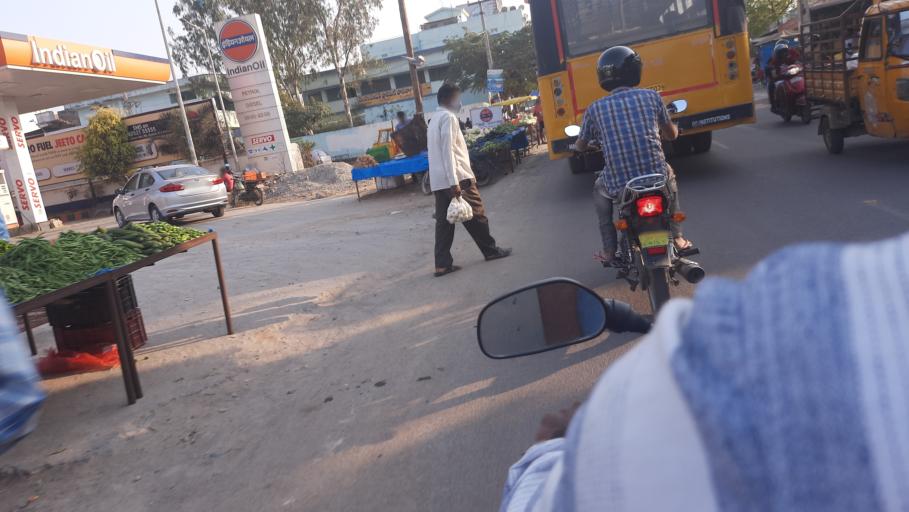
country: IN
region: Telangana
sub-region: Rangareddi
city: Secunderabad
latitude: 17.5086
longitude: 78.5412
